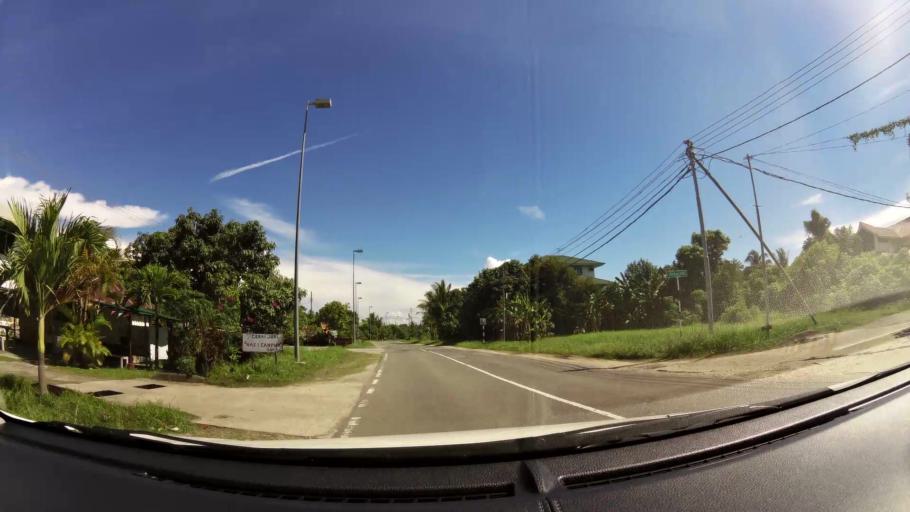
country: BN
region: Brunei and Muara
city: Bandar Seri Begawan
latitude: 5.0073
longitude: 115.0588
